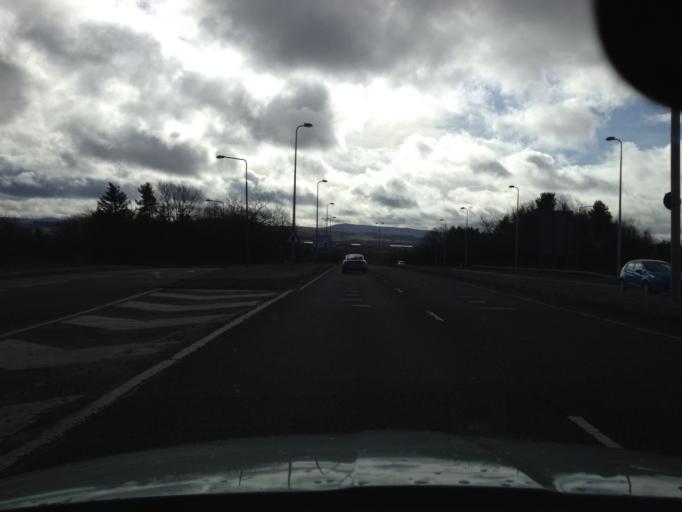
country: GB
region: Scotland
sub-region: West Lothian
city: Livingston
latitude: 55.9003
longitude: -3.5104
